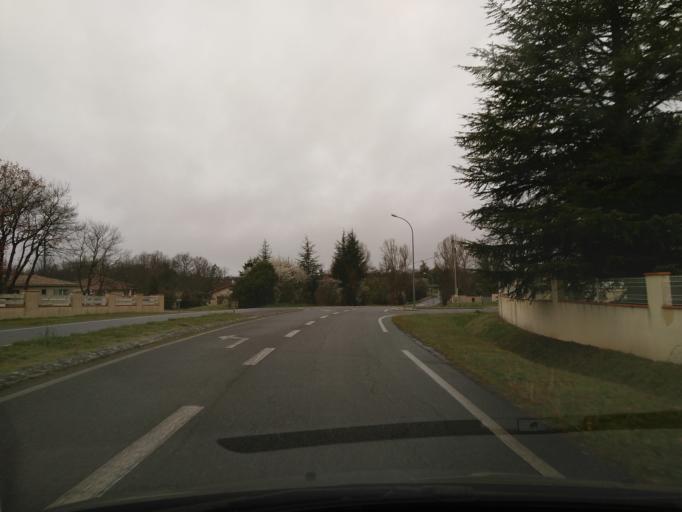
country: FR
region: Midi-Pyrenees
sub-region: Departement de la Haute-Garonne
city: Rieux-Volvestre
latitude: 43.2543
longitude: 1.1967
